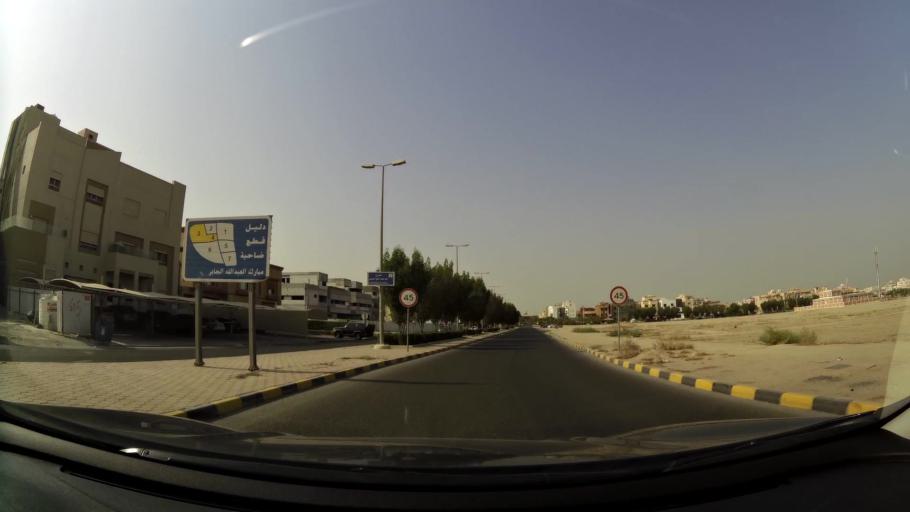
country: KW
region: Mubarak al Kabir
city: Sabah as Salim
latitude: 29.2750
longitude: 48.0449
